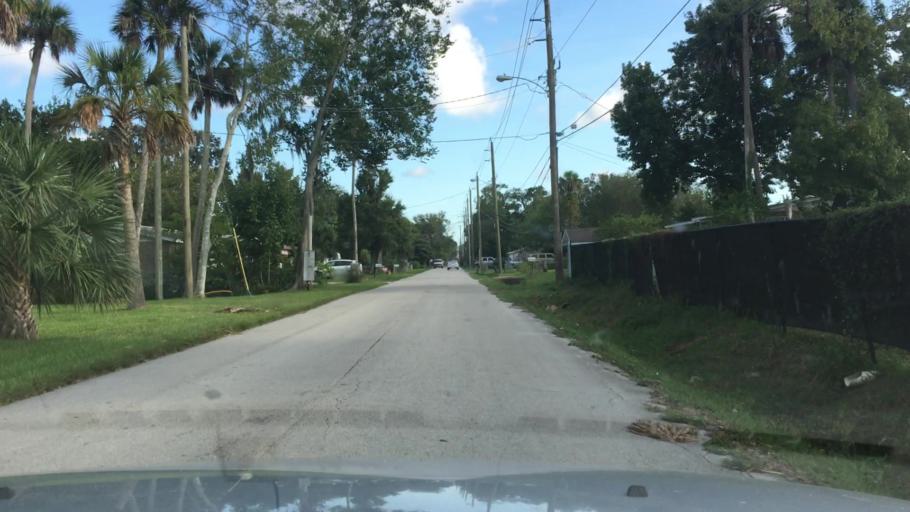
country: US
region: Florida
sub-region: Volusia County
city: Holly Hill
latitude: 29.2348
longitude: -81.0542
